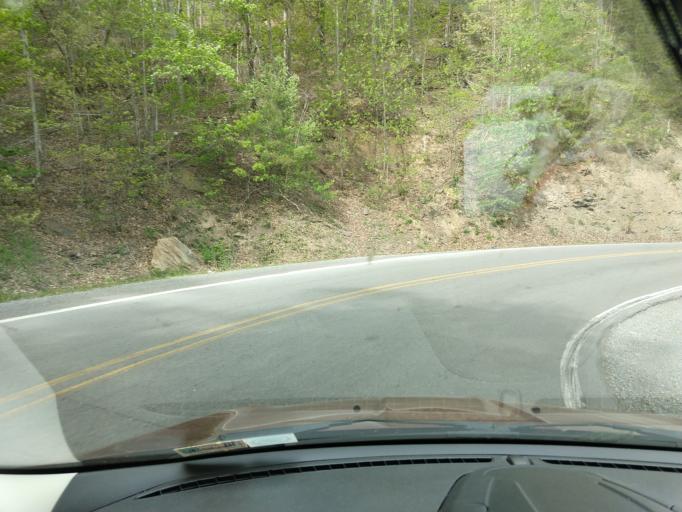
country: US
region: West Virginia
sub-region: McDowell County
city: Welch
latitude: 37.3621
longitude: -81.6467
